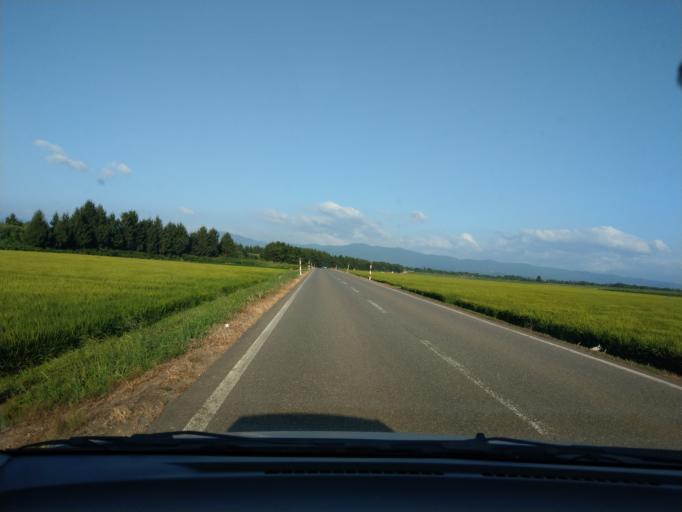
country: JP
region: Akita
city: Omagari
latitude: 39.4052
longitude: 140.4510
